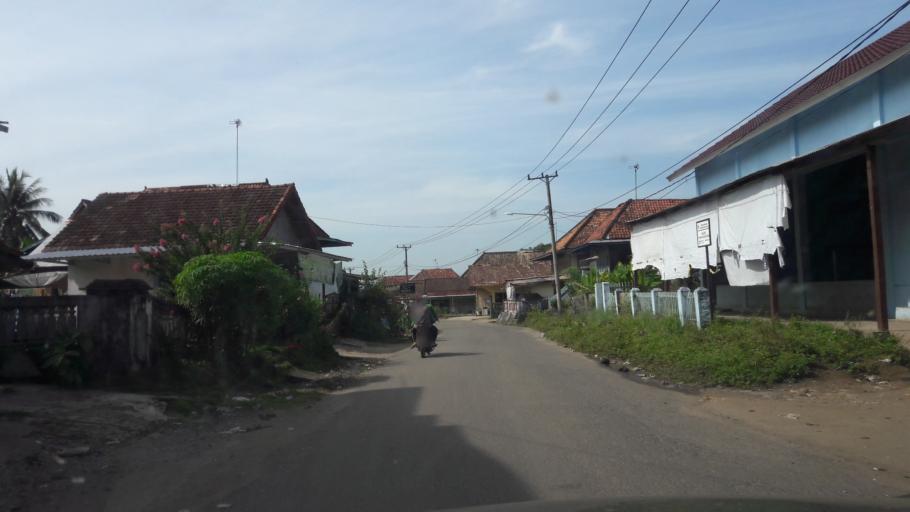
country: ID
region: South Sumatra
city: Gunungmenang
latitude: -3.3332
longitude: 104.0974
